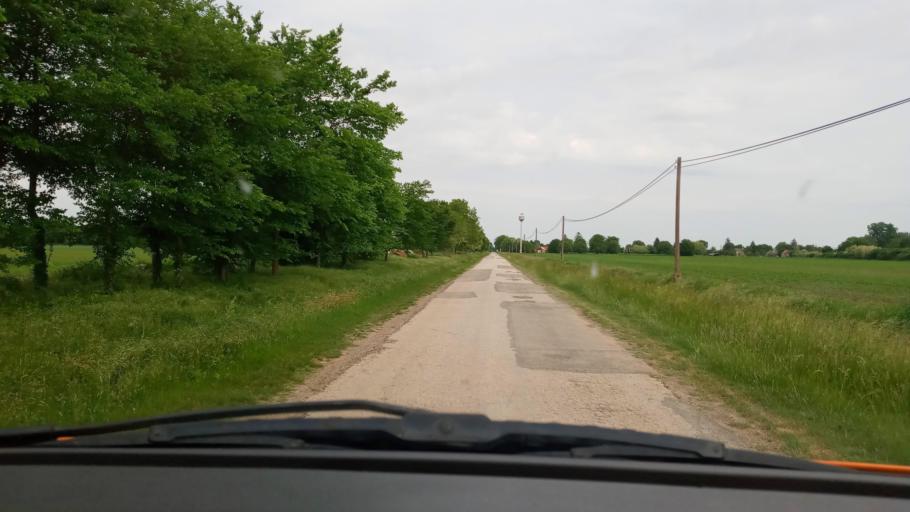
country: HU
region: Baranya
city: Vajszlo
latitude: 45.9220
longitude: 18.0241
